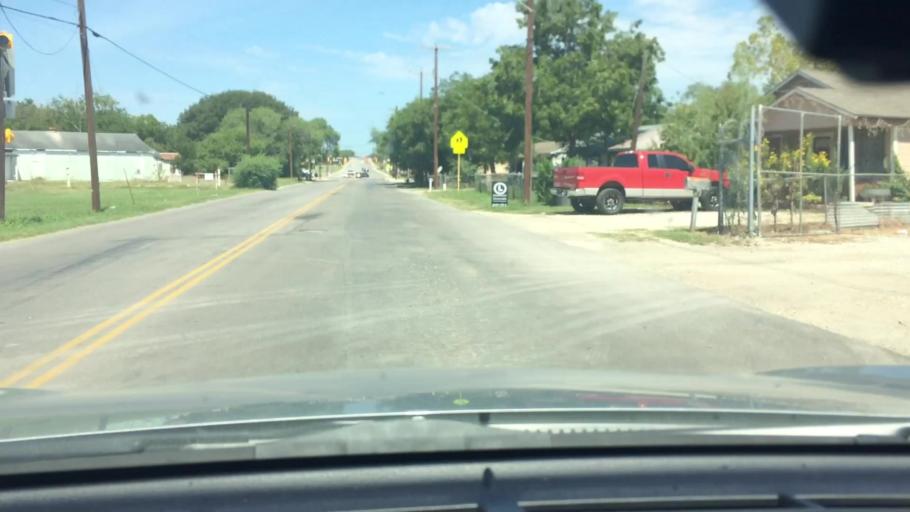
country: US
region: Texas
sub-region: Bexar County
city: San Antonio
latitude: 29.3968
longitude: -98.4343
